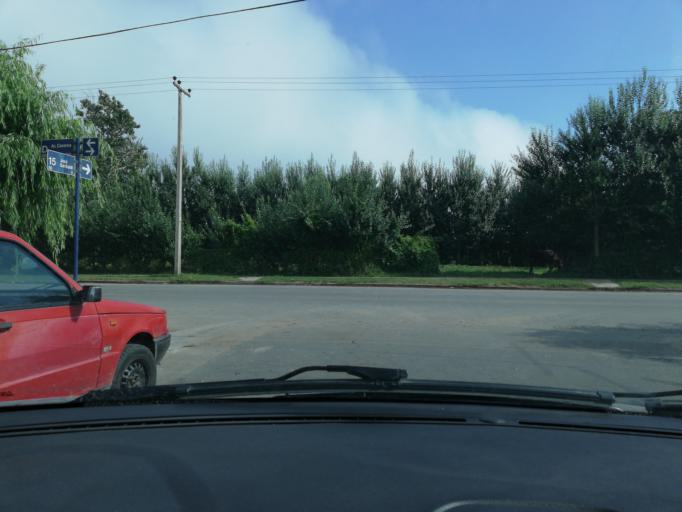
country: AR
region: Buenos Aires
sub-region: Partido de Balcarce
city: Balcarce
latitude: -37.8366
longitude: -58.2659
